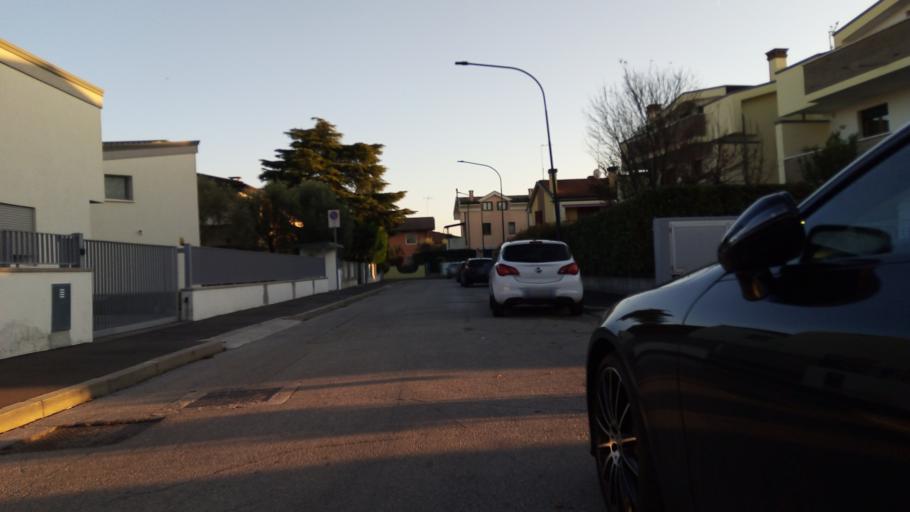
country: IT
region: Veneto
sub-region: Provincia di Padova
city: Abano Terme
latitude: 45.3694
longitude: 11.7952
